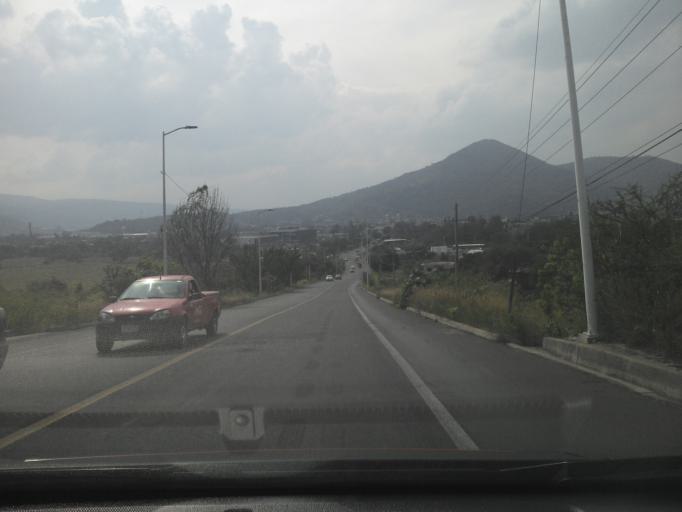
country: MX
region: Jalisco
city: Tlajomulco de Zuniga
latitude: 20.4790
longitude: -103.4353
